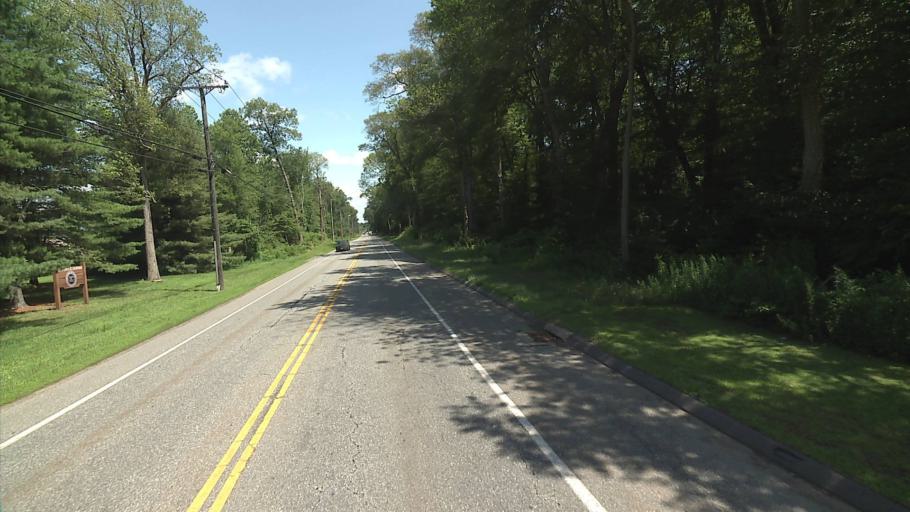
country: US
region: Connecticut
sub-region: Middlesex County
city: Old Saybrook
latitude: 41.3154
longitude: -72.3823
